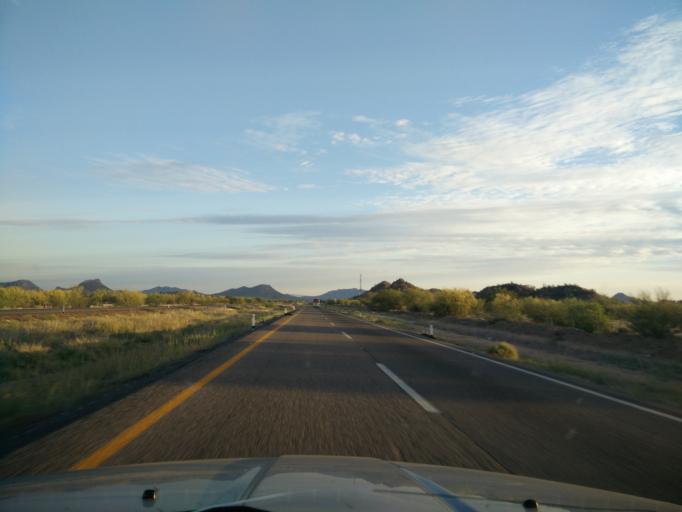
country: MX
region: Sonora
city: Hermosillo
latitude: 28.8252
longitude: -110.9581
